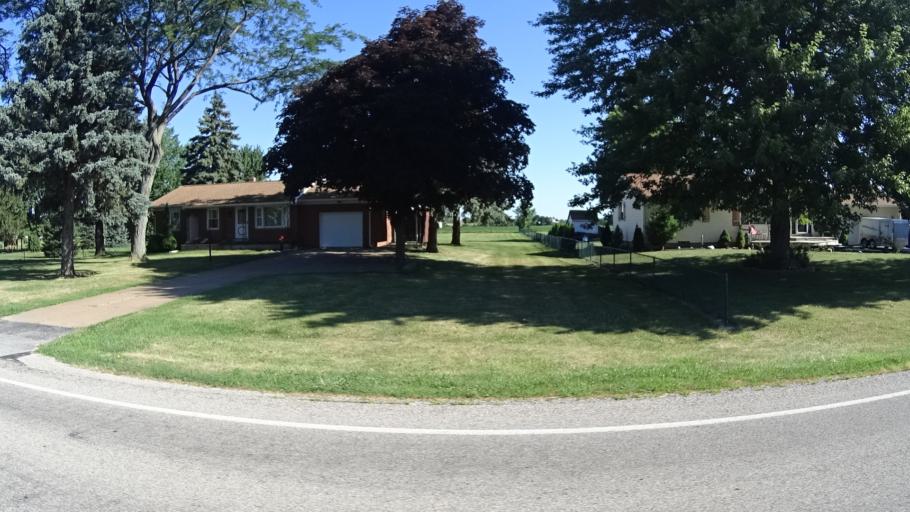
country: US
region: Ohio
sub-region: Erie County
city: Sandusky
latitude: 41.3970
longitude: -82.7280
